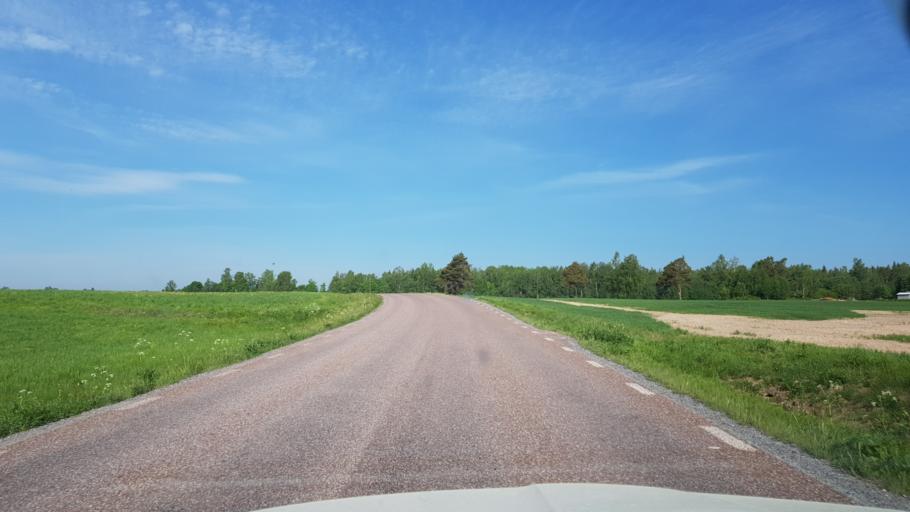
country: SE
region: Dalarna
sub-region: Borlange Kommun
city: Ornas
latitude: 60.4255
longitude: 15.6412
